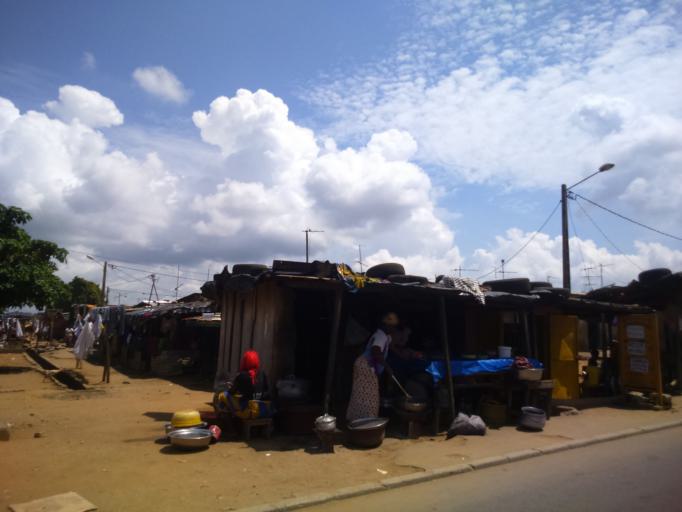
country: CI
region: Lagunes
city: Abidjan
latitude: 5.3525
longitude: -4.0874
